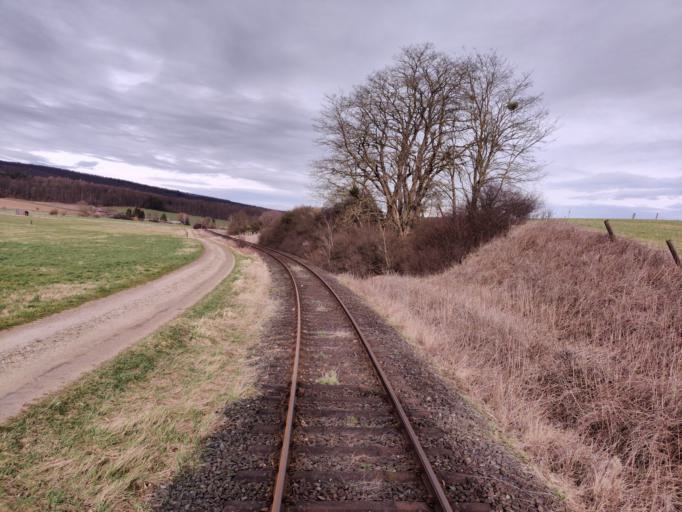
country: DE
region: Lower Saxony
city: Bockenem
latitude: 52.0391
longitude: 10.1225
